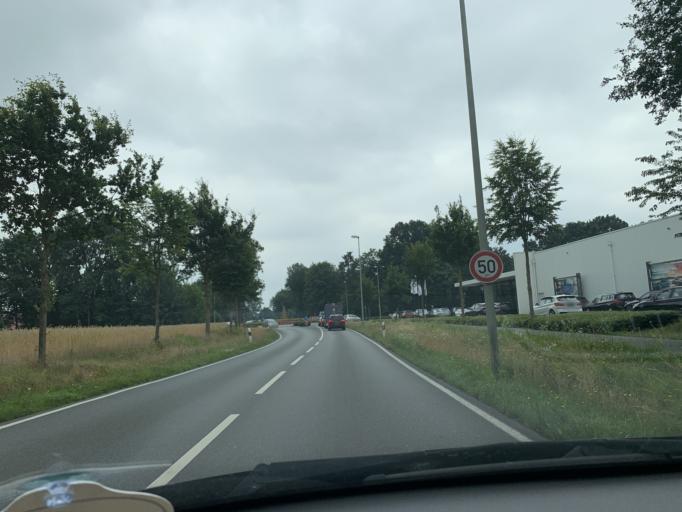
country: DE
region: North Rhine-Westphalia
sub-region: Regierungsbezirk Munster
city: Warendorf
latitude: 51.9588
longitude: 8.0102
